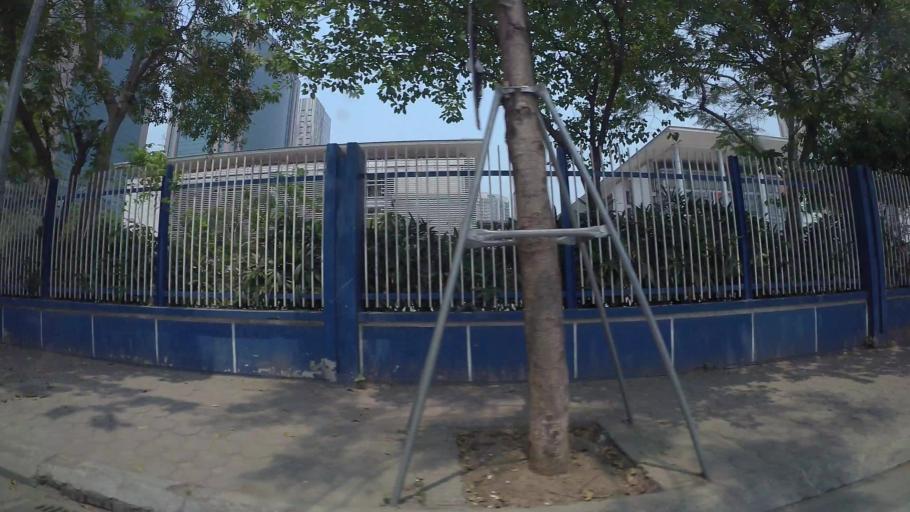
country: VN
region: Ha Noi
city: Thanh Xuan
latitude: 21.0065
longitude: 105.7970
